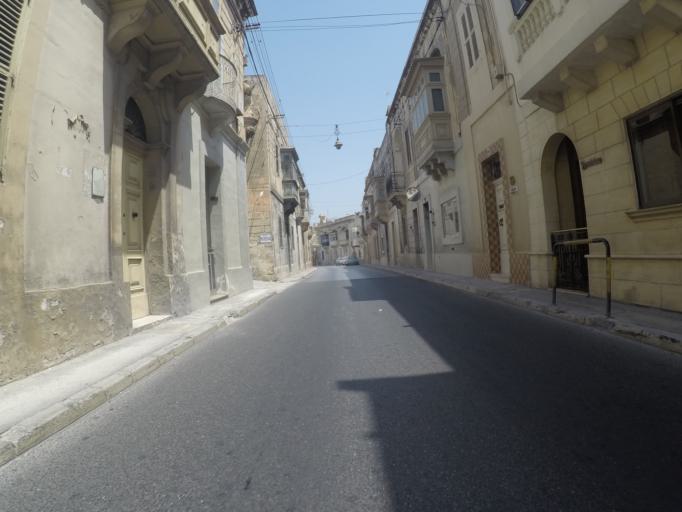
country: MT
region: Ir-Rabat
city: Rabat
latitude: 35.8775
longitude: 14.3998
